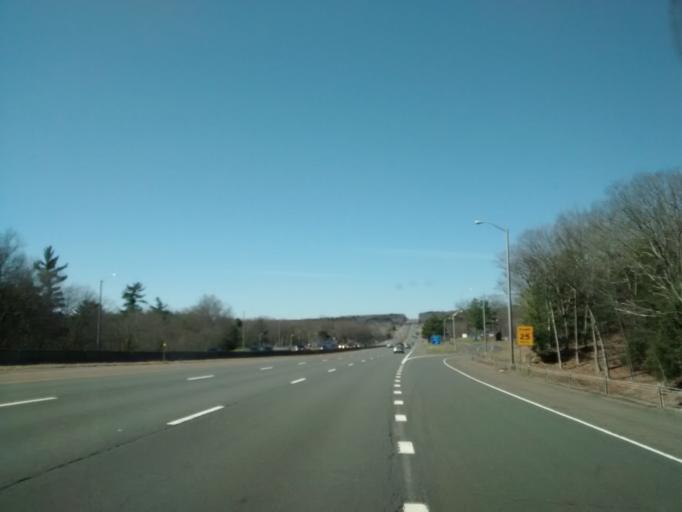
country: US
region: Connecticut
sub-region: Tolland County
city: Stafford Springs
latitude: 41.8952
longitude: -72.2928
